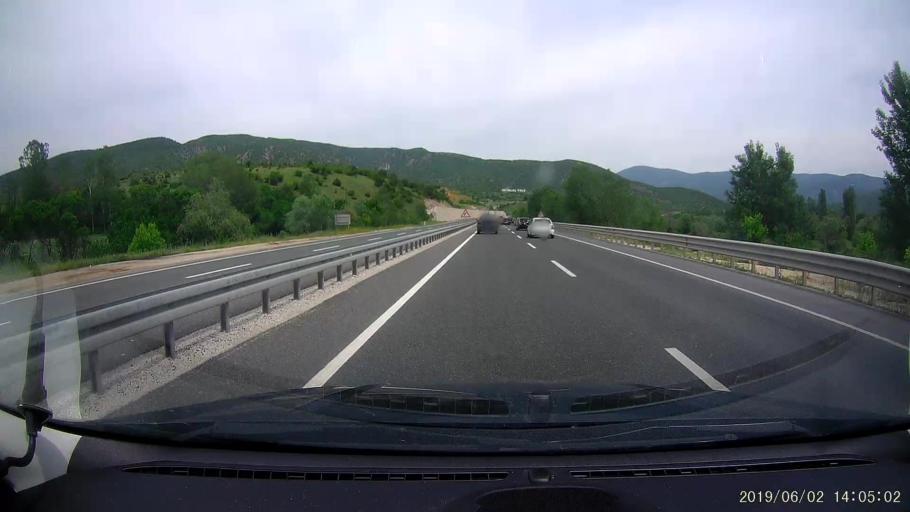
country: TR
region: Cankiri
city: Ilgaz
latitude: 40.9029
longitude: 33.6626
